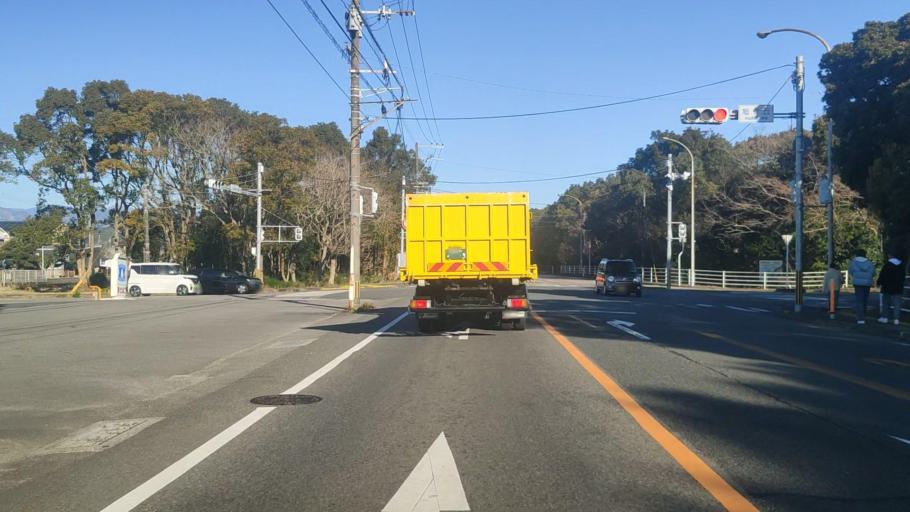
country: JP
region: Miyazaki
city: Nobeoka
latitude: 32.5286
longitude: 131.6818
